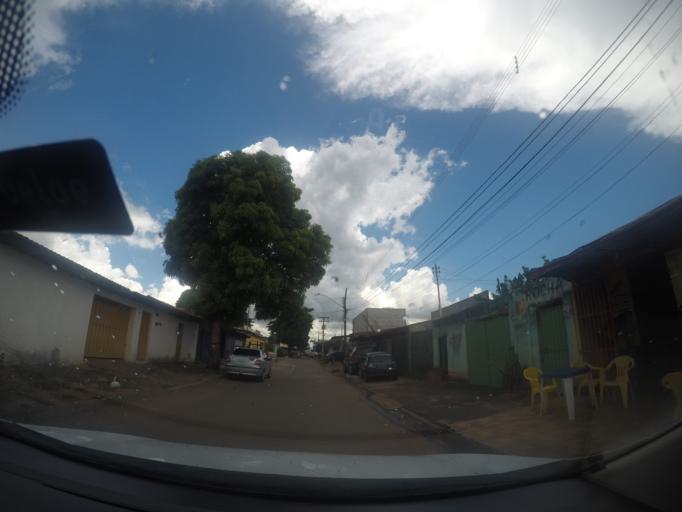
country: BR
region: Goias
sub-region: Goiania
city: Goiania
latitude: -16.6934
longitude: -49.3152
